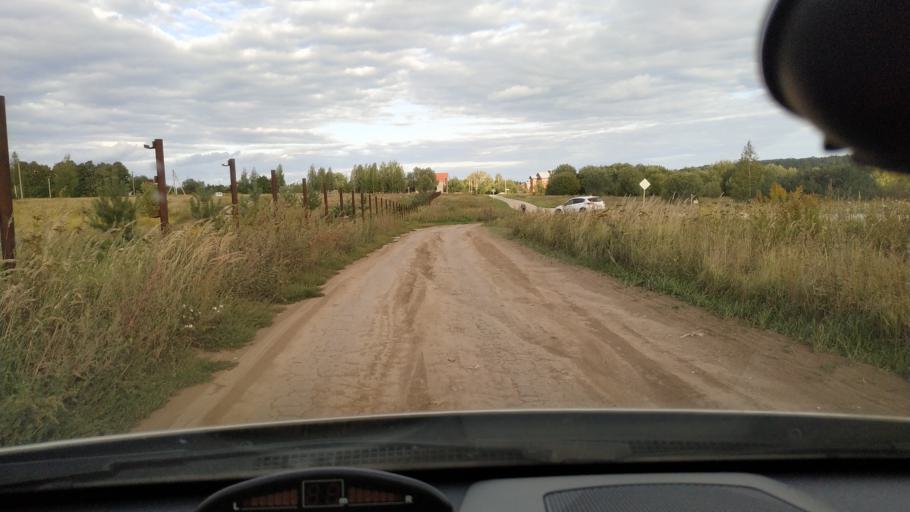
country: RU
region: Rjazan
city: Polyany
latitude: 54.5646
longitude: 39.8730
